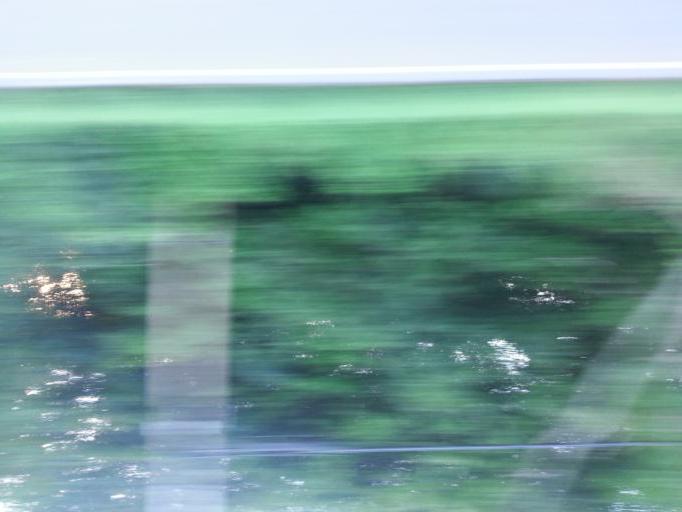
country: US
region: Tennessee
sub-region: Loudon County
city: Lenoir City
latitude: 35.8581
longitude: -84.2260
